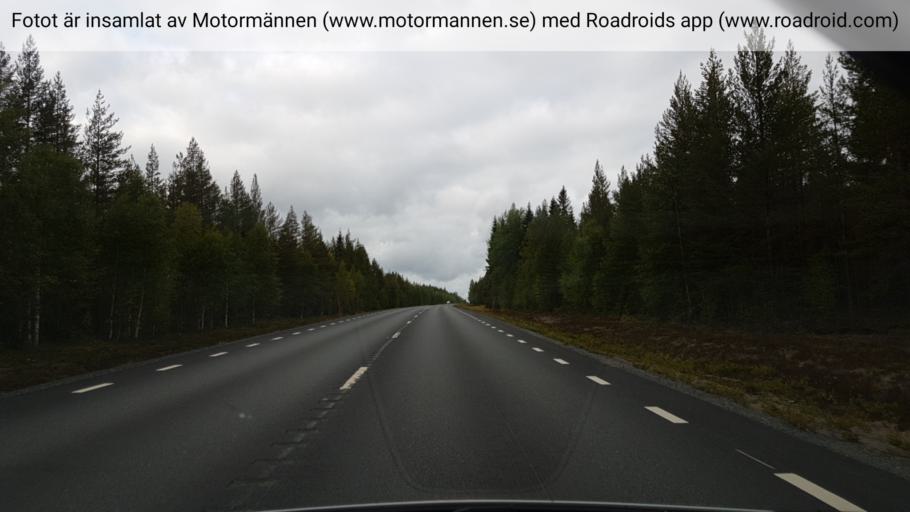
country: SE
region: Vaesterbotten
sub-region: Norsjo Kommun
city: Norsjoe
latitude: 64.9692
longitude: 19.7699
